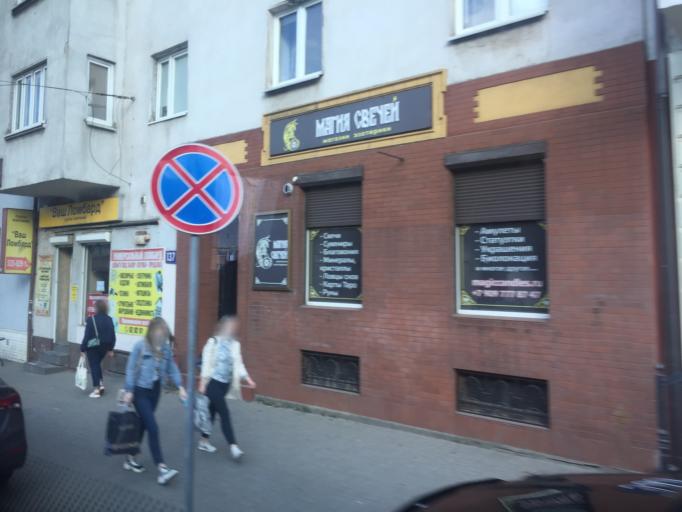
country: RU
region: Kaliningrad
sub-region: Gorod Kaliningrad
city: Kaliningrad
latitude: 54.6981
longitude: 20.5030
